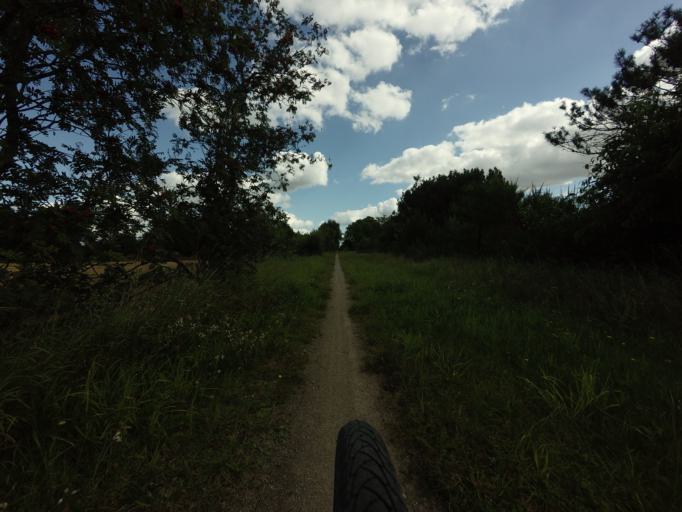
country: DK
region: Central Jutland
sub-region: Ikast-Brande Kommune
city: Brande
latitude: 55.9772
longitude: 9.2374
